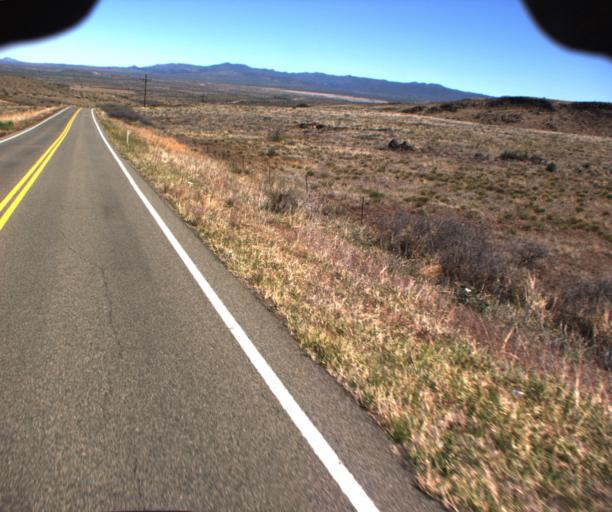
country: US
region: Arizona
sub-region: Yavapai County
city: Congress
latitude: 34.3369
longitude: -112.6865
